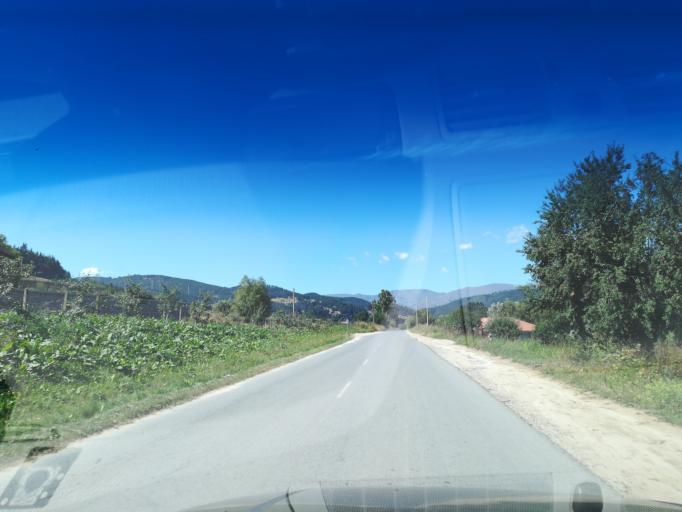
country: BG
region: Sofiya
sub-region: Obshtina Koprivshtitsa
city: Koprivshtitsa
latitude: 42.6215
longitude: 24.3685
